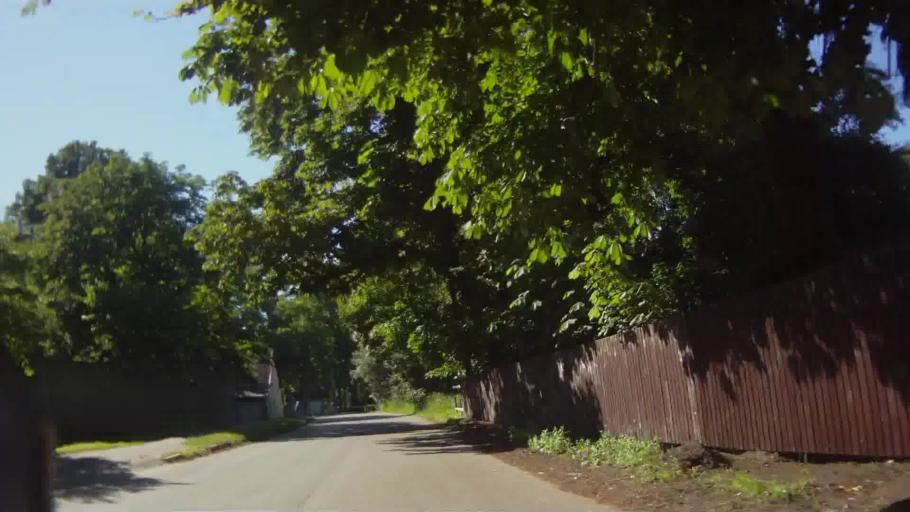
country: LV
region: Riga
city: Riga
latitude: 56.9133
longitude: 24.0884
